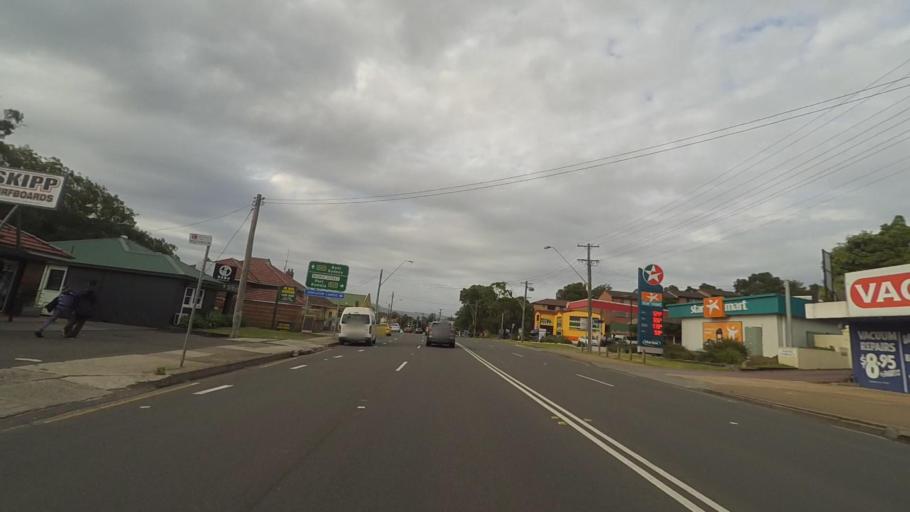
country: AU
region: New South Wales
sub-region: Wollongong
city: Gwynneville
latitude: -34.4155
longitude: 150.8928
